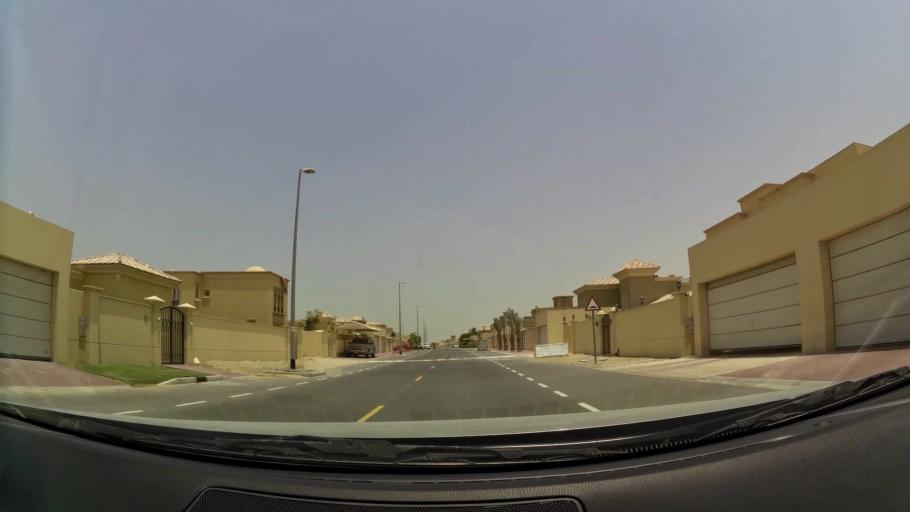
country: AE
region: Dubai
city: Dubai
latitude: 25.0848
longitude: 55.2475
